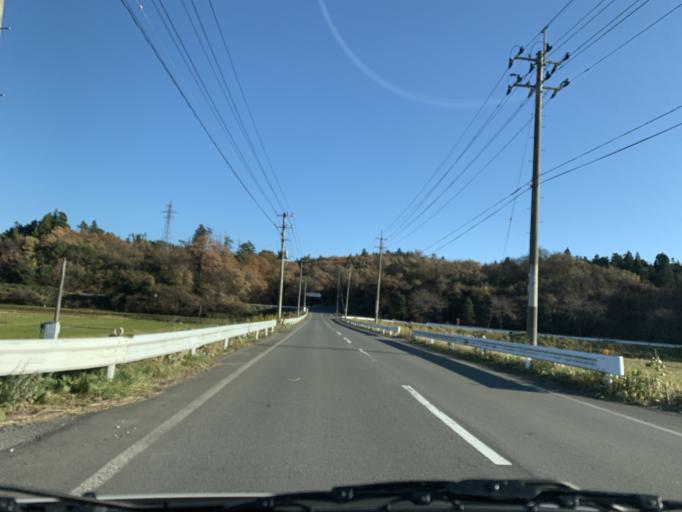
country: JP
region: Iwate
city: Mizusawa
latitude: 39.2011
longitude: 141.1931
